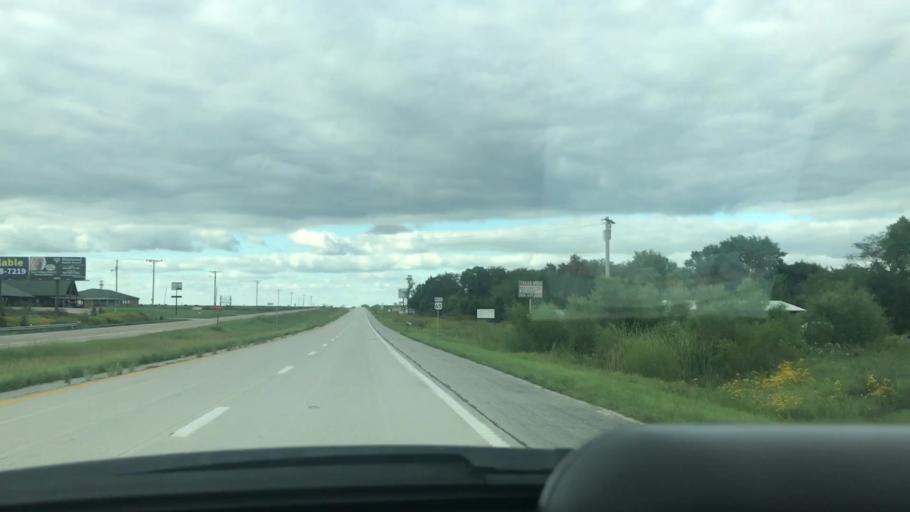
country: US
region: Missouri
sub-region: Benton County
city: Lincoln
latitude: 38.3482
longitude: -93.3400
